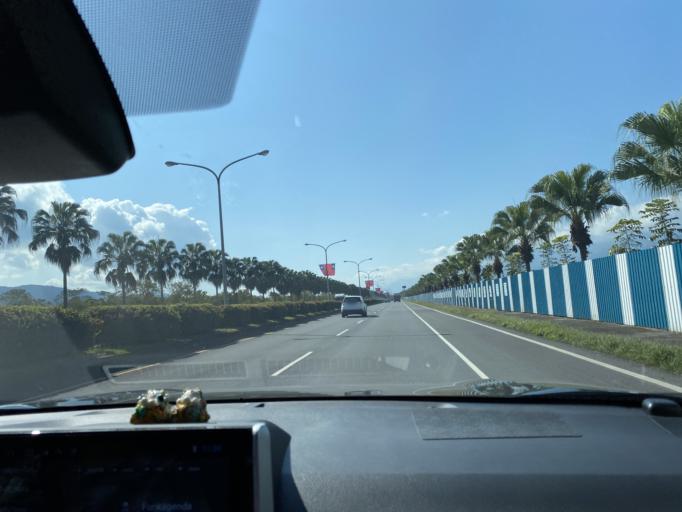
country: TW
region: Taiwan
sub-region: Hualien
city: Hualian
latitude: 23.8707
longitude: 121.5354
